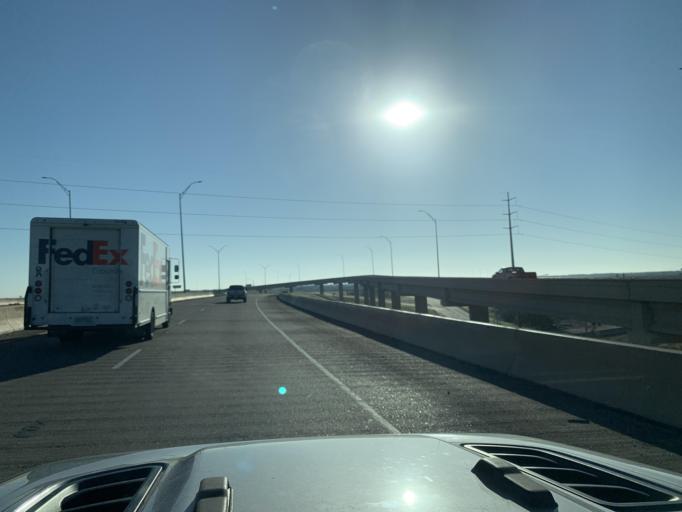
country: US
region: Texas
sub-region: Nueces County
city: Corpus Christi
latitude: 27.7845
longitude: -97.4868
